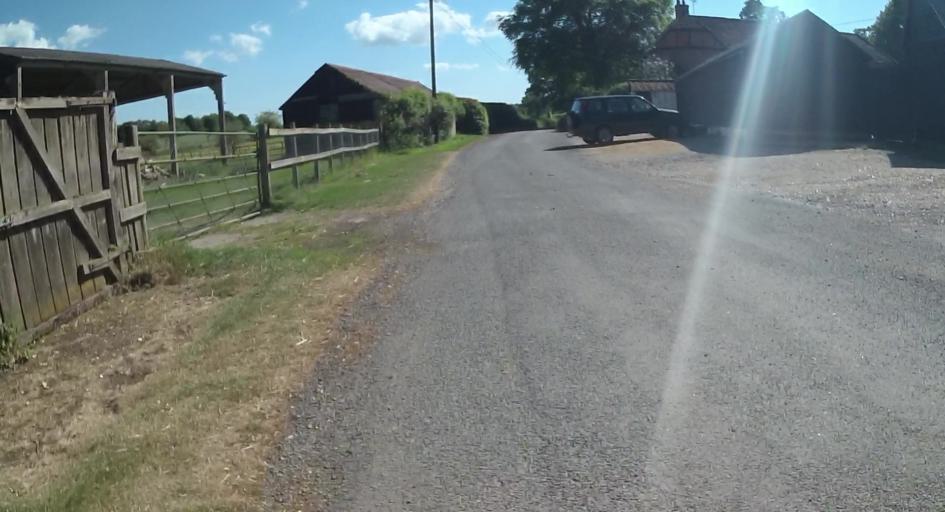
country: GB
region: England
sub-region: Hampshire
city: Old Basing
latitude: 51.2415
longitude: -1.0263
